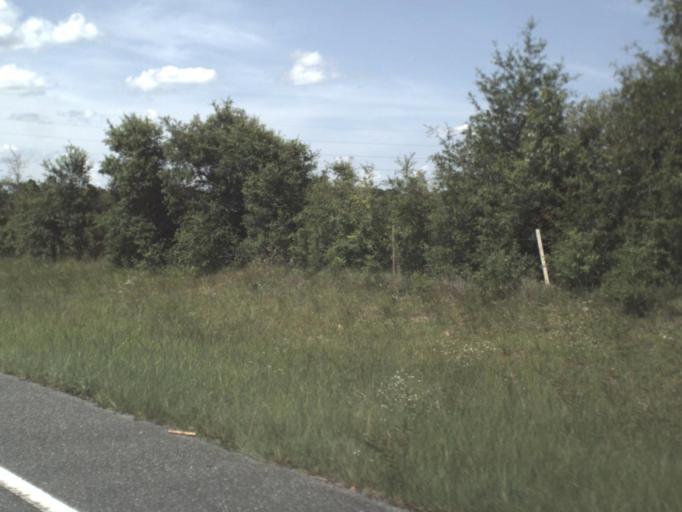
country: US
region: Florida
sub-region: Gilchrist County
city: Trenton
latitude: 29.7502
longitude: -82.7406
